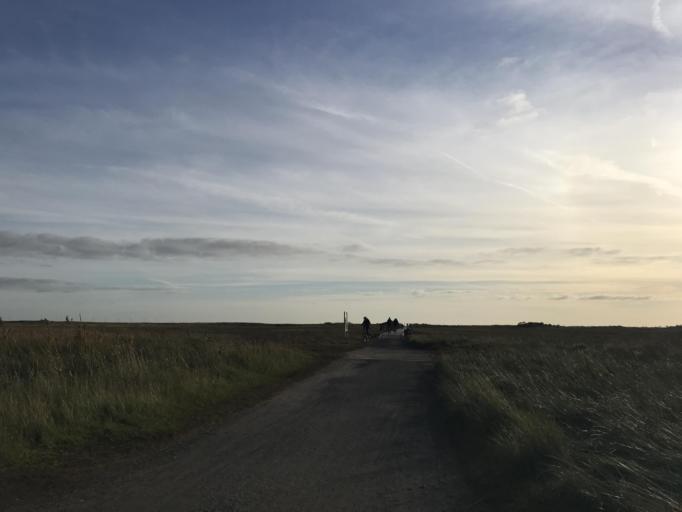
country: DE
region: Lower Saxony
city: Borkum
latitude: 53.5714
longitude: 6.7044
